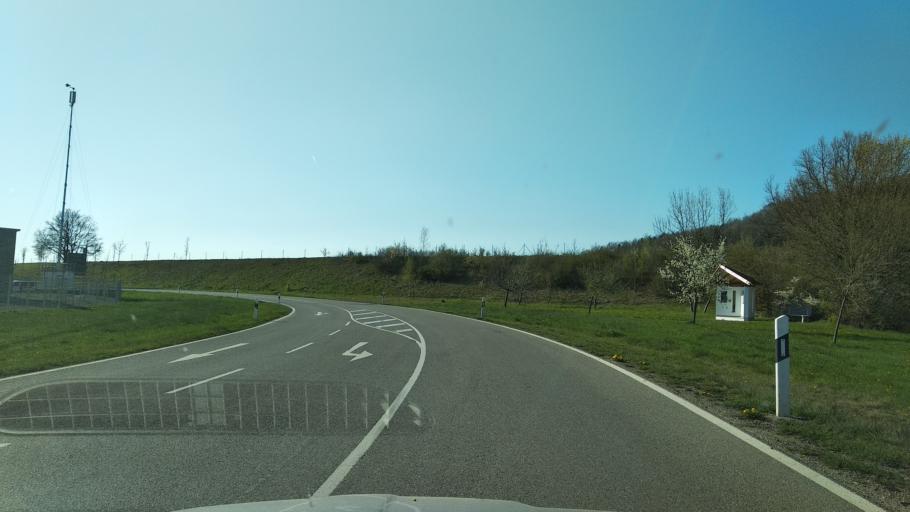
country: DE
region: Bavaria
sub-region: Swabia
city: Westerheim
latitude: 48.0237
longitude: 10.3054
